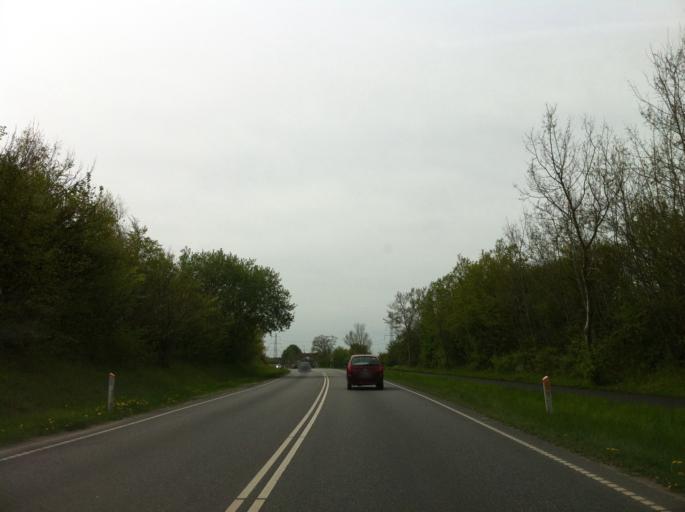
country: DK
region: Capital Region
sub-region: Frederikssund Kommune
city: Slangerup
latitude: 55.8356
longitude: 12.1671
